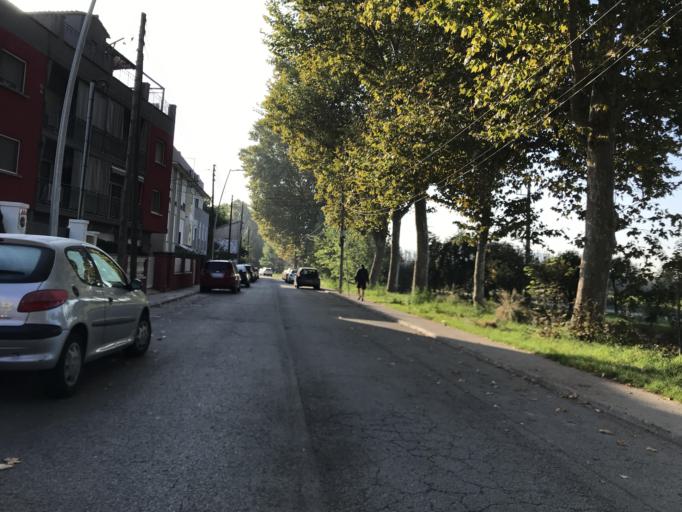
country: ES
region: Catalonia
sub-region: Provincia de Barcelona
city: Mollet del Valles
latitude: 41.5557
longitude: 2.2200
